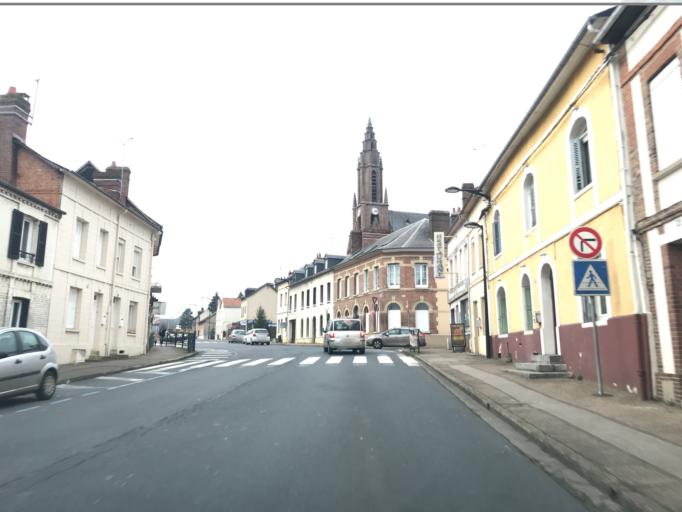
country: FR
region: Haute-Normandie
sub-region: Departement de l'Eure
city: Fleury-sur-Andelle
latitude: 49.3622
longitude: 1.3557
